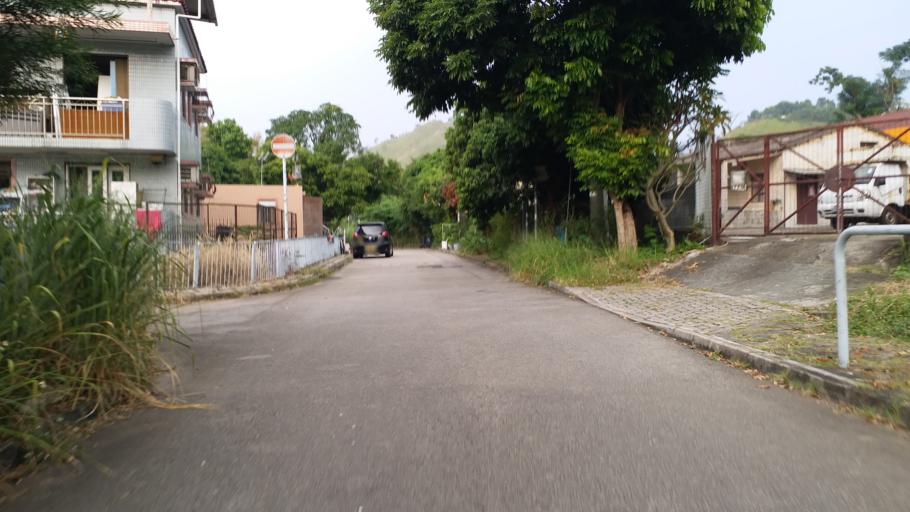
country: HK
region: Yuen Long
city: Yuen Long Kau Hui
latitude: 22.4542
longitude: 114.0111
